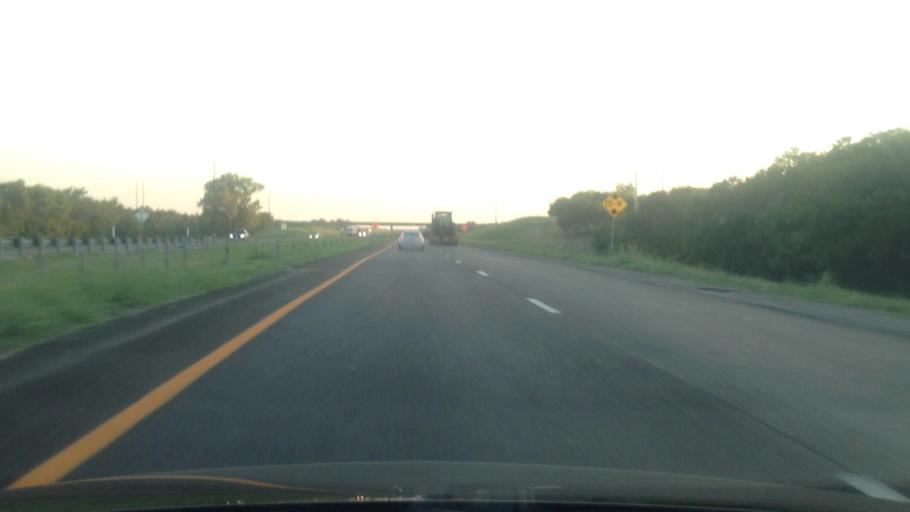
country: US
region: Texas
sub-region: Denton County
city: Argyle
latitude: 33.1756
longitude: -97.1789
